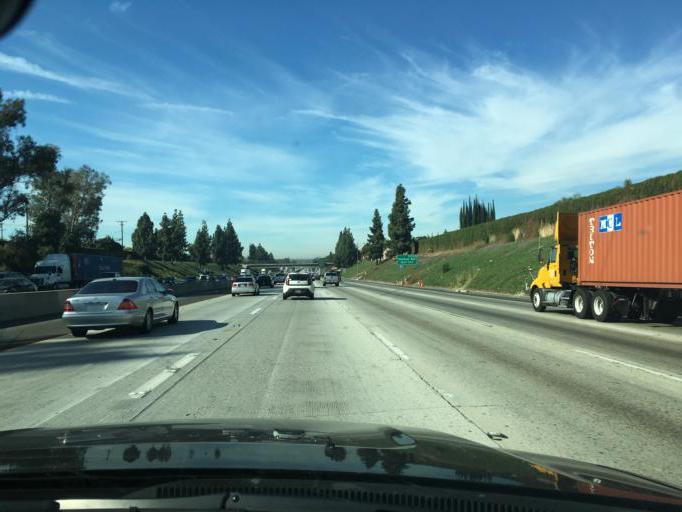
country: US
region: California
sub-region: San Bernardino County
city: Chino
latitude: 34.0304
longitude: -117.6757
